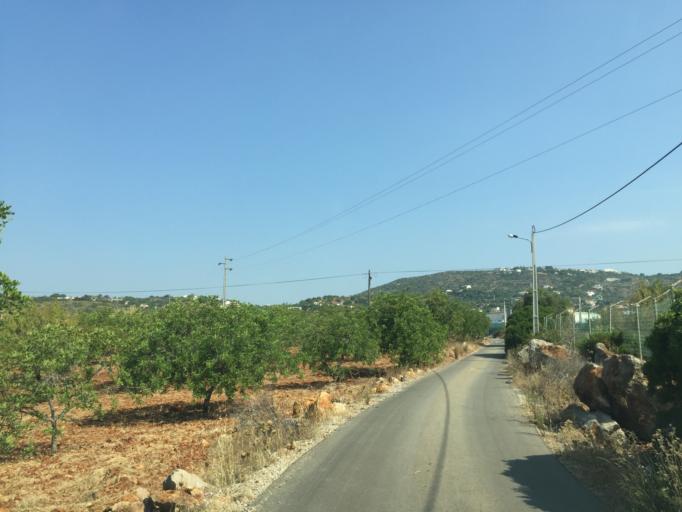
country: PT
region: Faro
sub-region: Loule
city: Almancil
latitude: 37.0957
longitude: -8.0008
